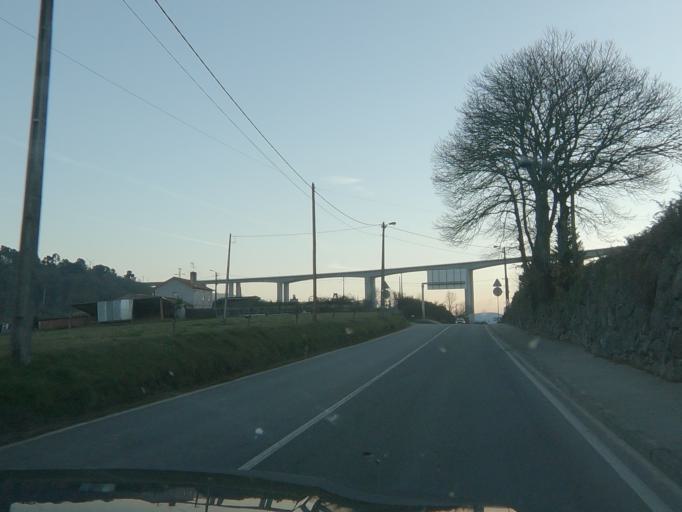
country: PT
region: Vila Real
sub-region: Vila Pouca de Aguiar
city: Vila Pouca de Aguiar
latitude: 41.4890
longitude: -7.6495
